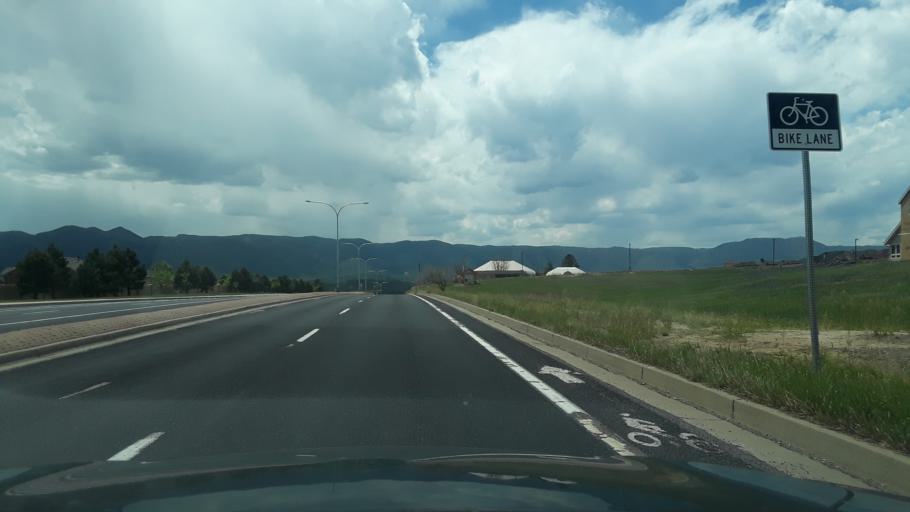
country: US
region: Colorado
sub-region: El Paso County
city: Gleneagle
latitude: 39.0273
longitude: -104.8080
